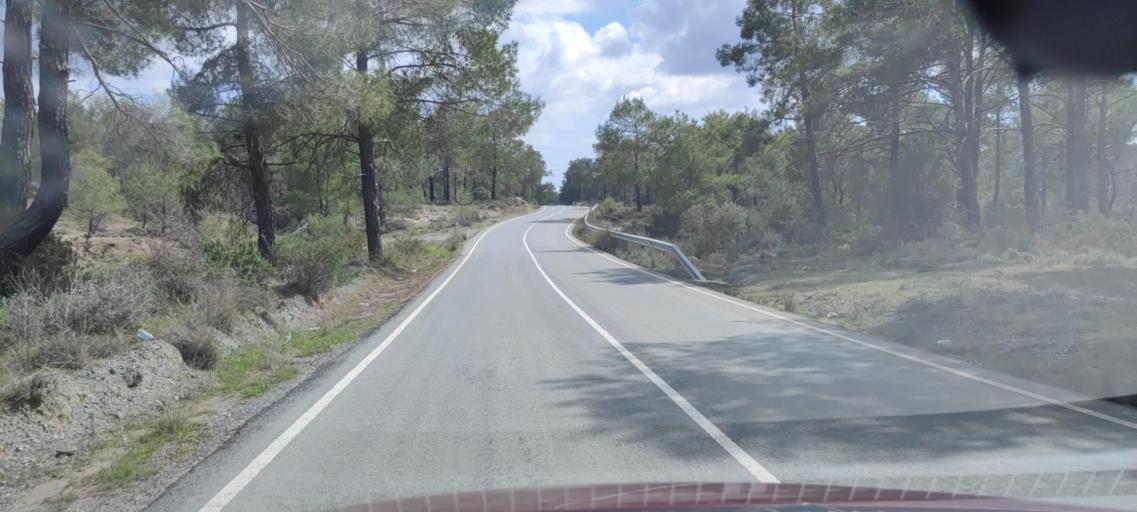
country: CY
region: Larnaka
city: Kornos
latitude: 34.9264
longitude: 33.3453
